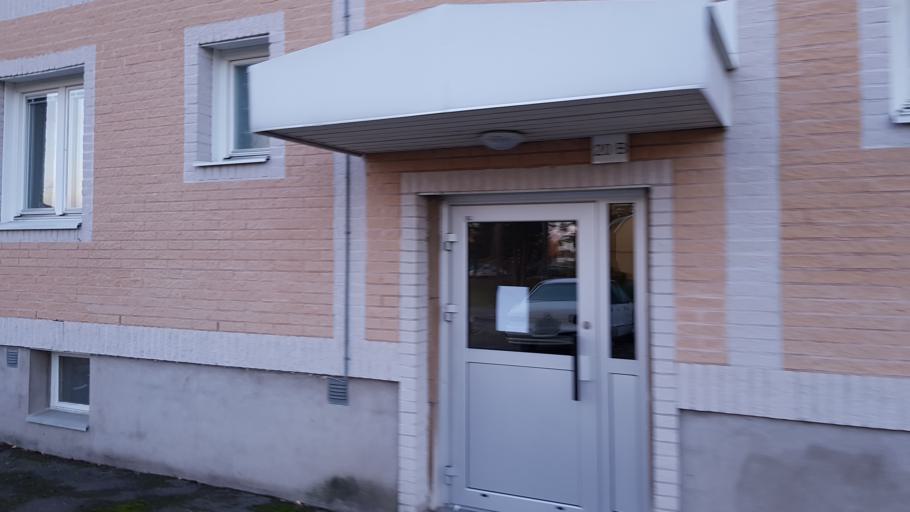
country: SE
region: Vaermland
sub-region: Hammaro Kommun
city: Skoghall
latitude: 59.3231
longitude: 13.4721
